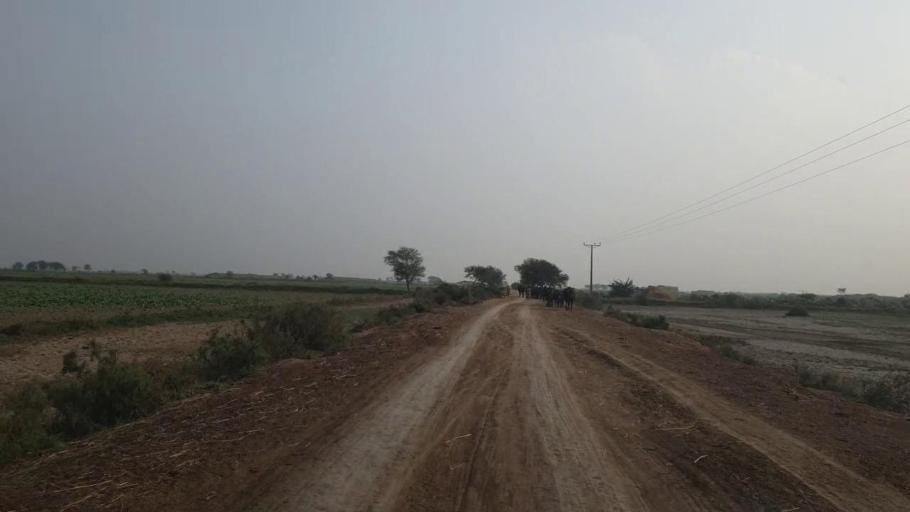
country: PK
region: Sindh
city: Mirpur Batoro
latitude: 24.5455
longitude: 68.4209
